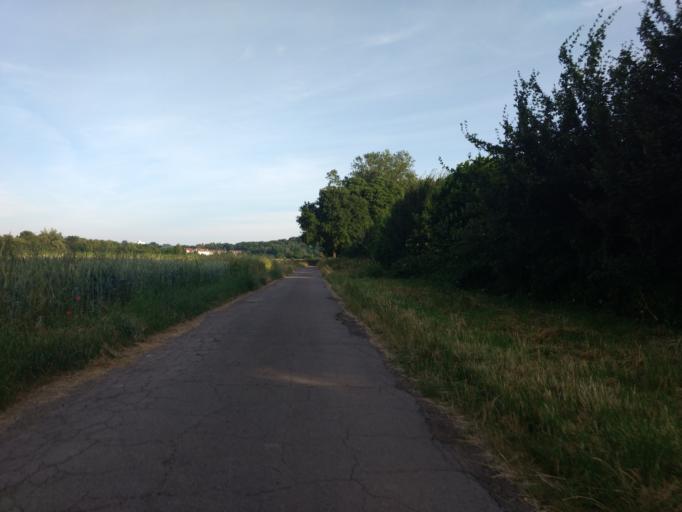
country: DE
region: Saarland
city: Wallerfangen
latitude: 49.3136
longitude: 6.7257
